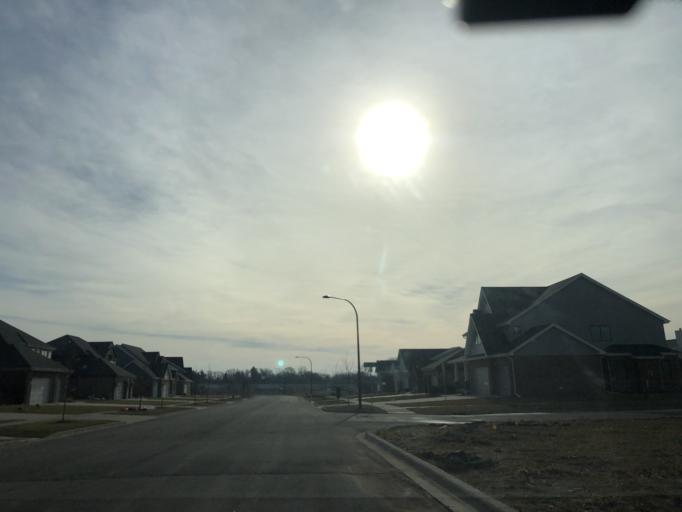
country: US
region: Illinois
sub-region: Cook County
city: Lemont
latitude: 41.7178
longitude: -88.0131
